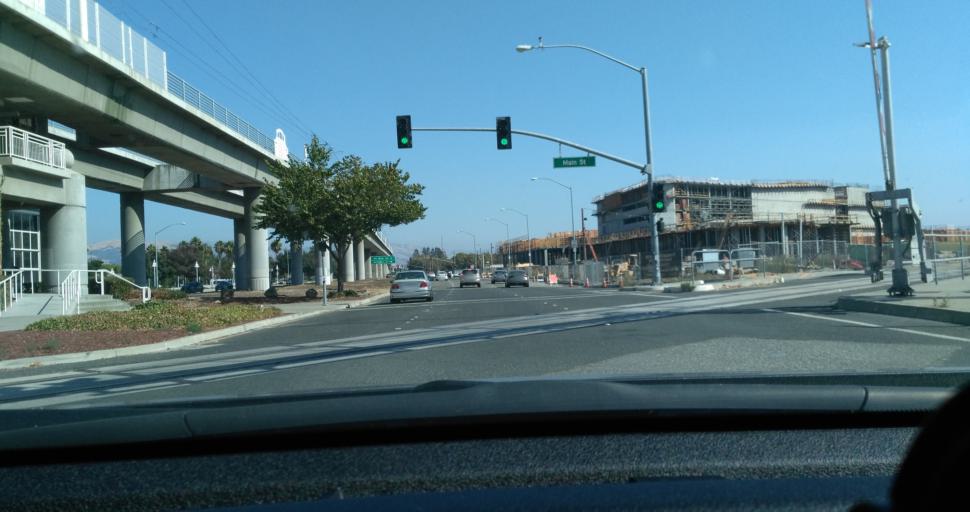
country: US
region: California
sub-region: Santa Clara County
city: Milpitas
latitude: 37.4139
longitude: -121.9017
